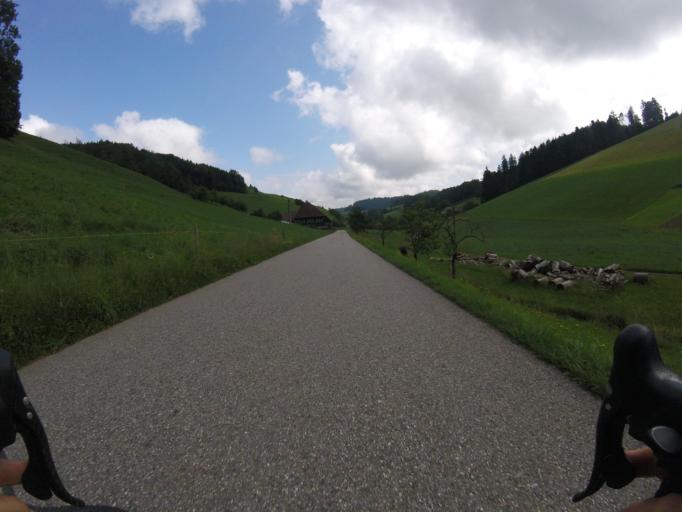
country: CH
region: Bern
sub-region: Emmental District
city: Krauchthal
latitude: 46.9967
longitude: 7.5893
